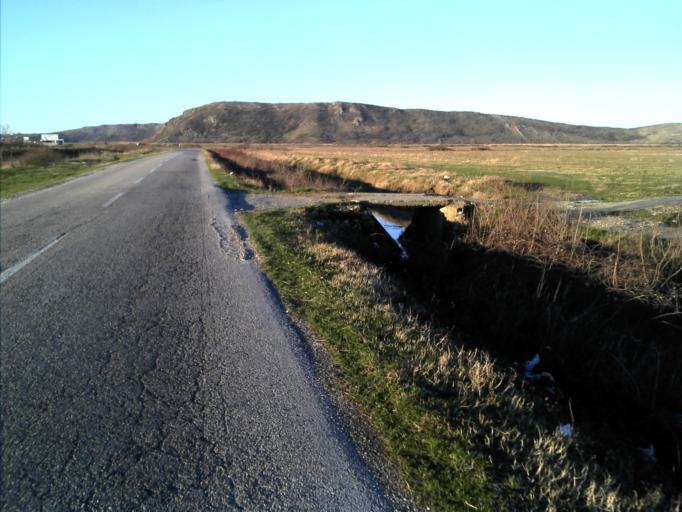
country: AL
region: Shkoder
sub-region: Rrethi i Shkodres
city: Dajc
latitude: 41.9460
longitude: 19.4491
